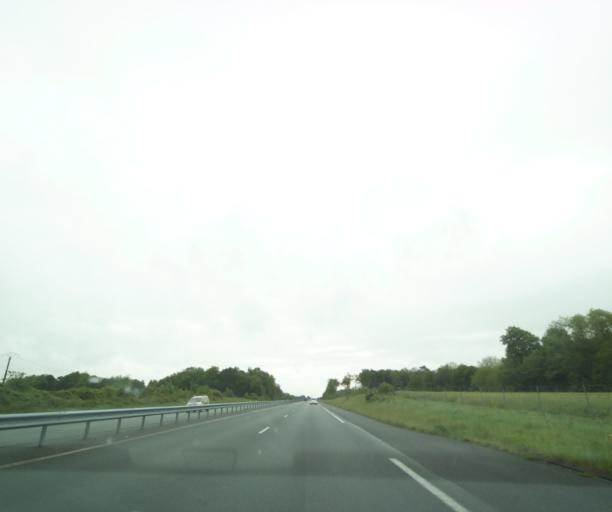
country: FR
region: Poitou-Charentes
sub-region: Departement de la Charente-Maritime
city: Chermignac
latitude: 45.7053
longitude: -0.7179
